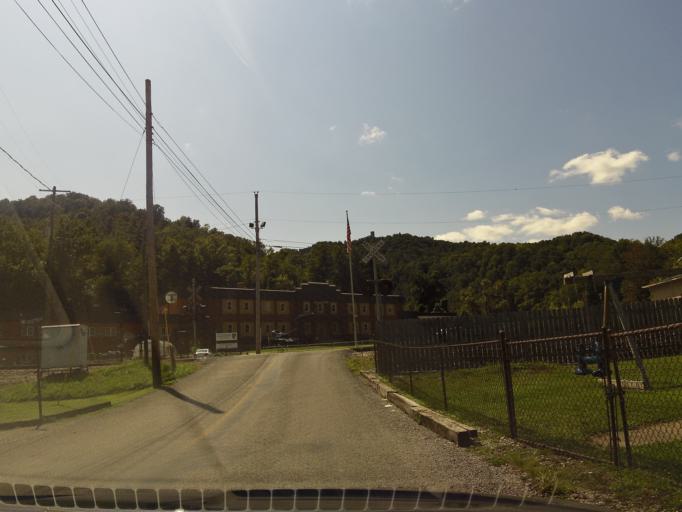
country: US
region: Kentucky
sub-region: Harlan County
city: Harlan
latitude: 36.8053
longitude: -83.3043
